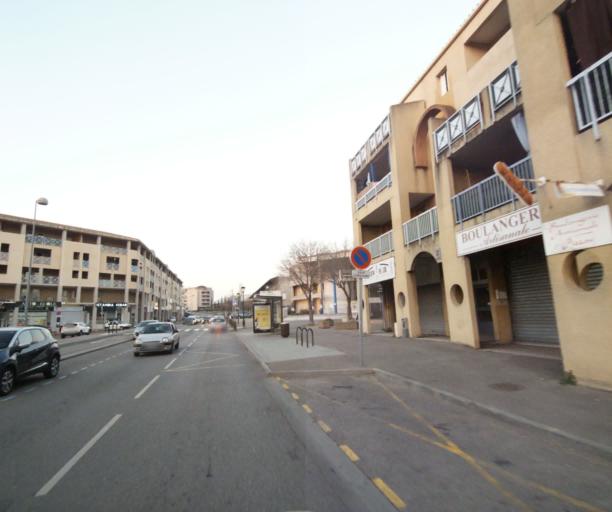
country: FR
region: Provence-Alpes-Cote d'Azur
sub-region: Departement des Bouches-du-Rhone
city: Saint-Victoret
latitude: 43.4241
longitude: 5.2715
